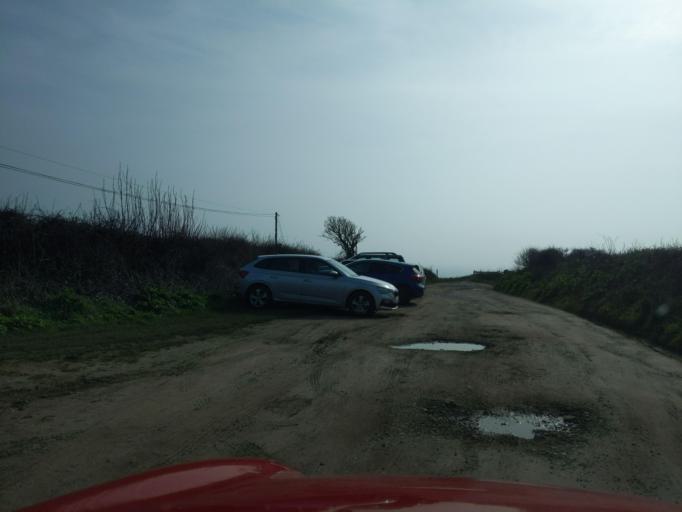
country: GB
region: England
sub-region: Devon
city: Salcombe
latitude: 50.2228
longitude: -3.7507
